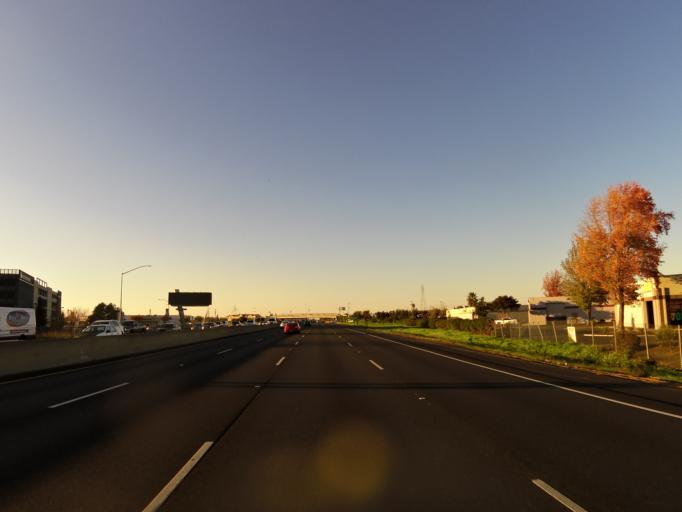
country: US
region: California
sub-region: Sacramento County
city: Florin
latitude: 38.4709
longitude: -121.4191
